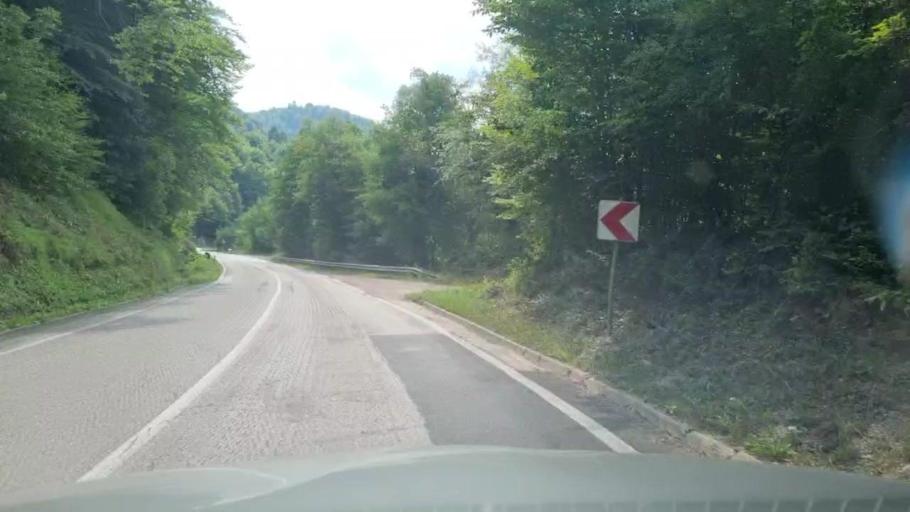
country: BA
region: Federation of Bosnia and Herzegovina
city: Kladanj
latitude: 44.2353
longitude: 18.7283
